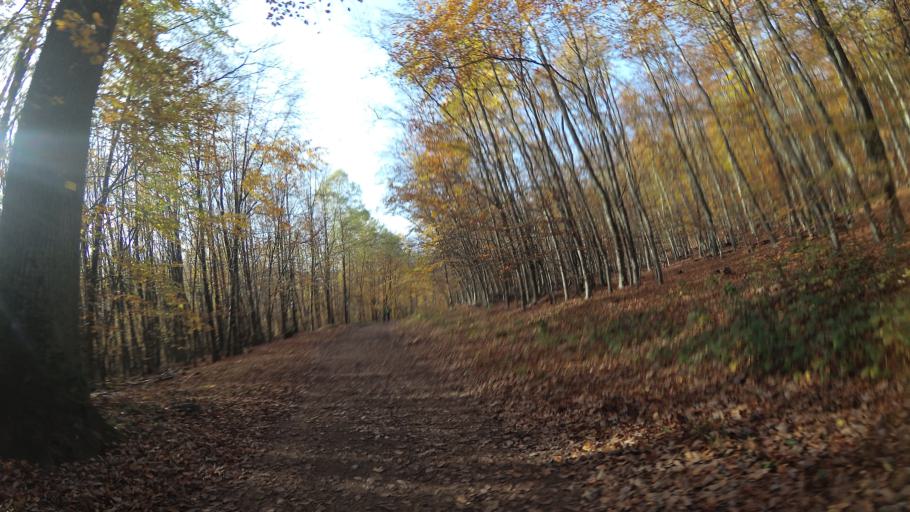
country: DE
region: Saarland
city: Hangard
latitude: 49.3726
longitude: 7.2324
